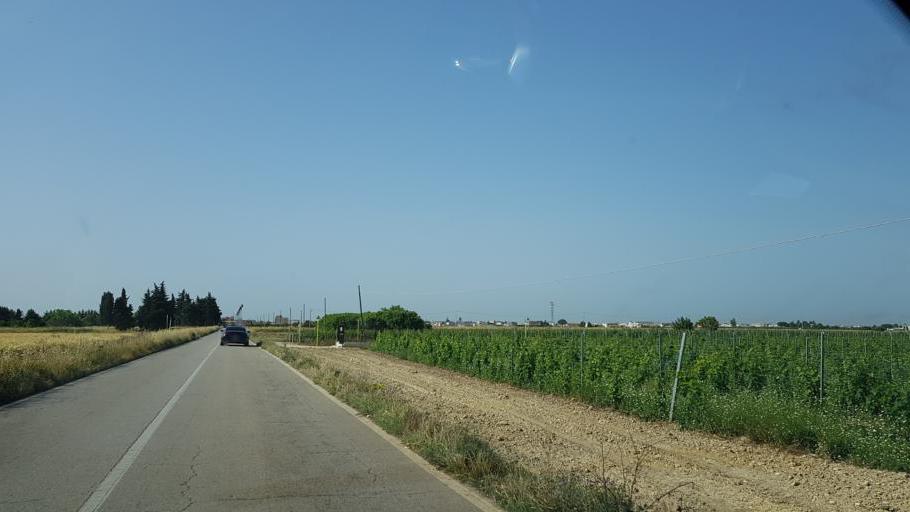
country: IT
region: Apulia
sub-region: Provincia di Brindisi
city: San Pancrazio Salentino
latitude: 40.4303
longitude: 17.8403
